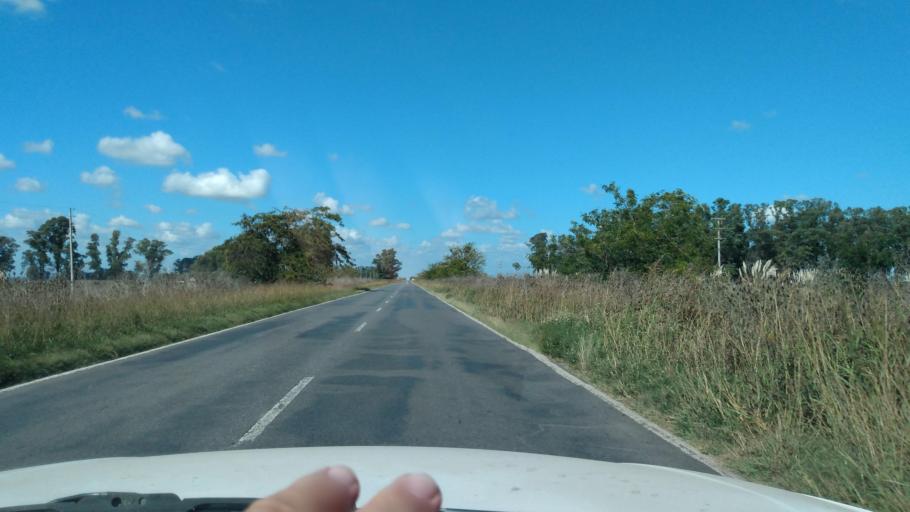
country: AR
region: Buenos Aires
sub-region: Partido de Mercedes
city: Mercedes
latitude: -34.7375
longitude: -59.3868
